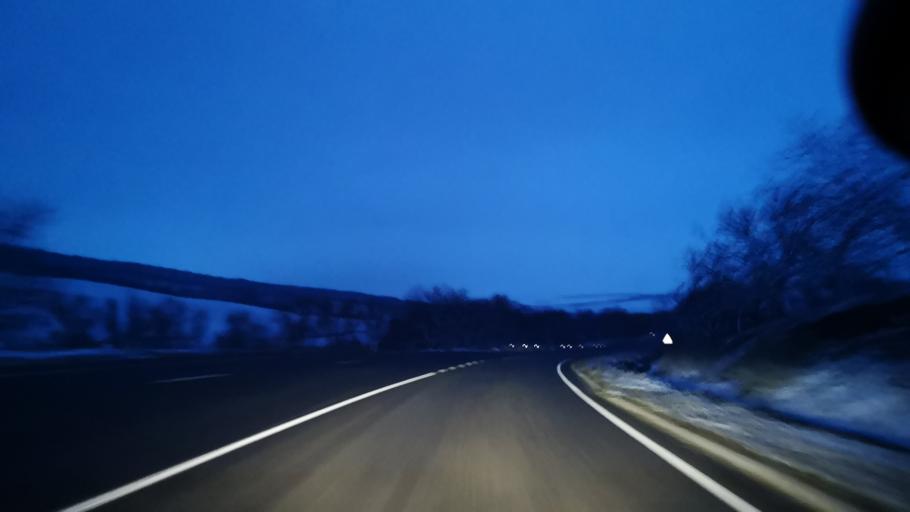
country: MD
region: Orhei
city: Orhei
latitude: 47.5081
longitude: 28.8018
